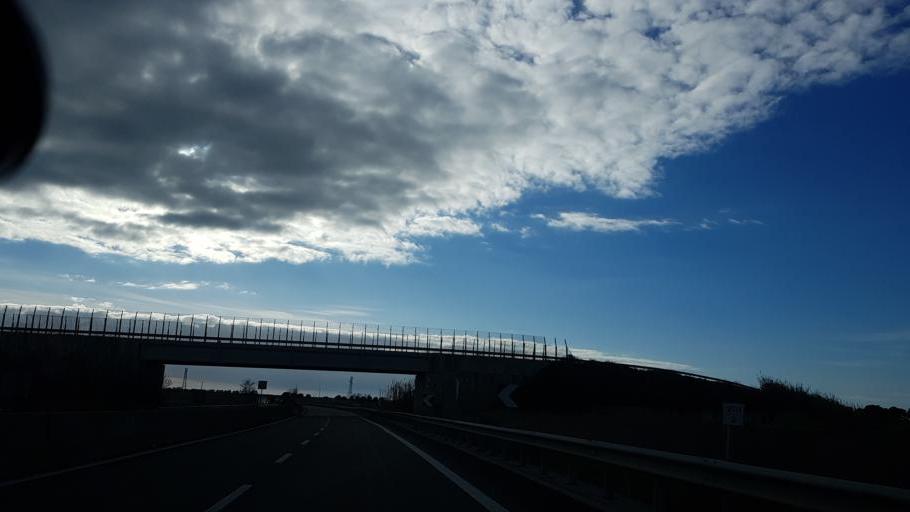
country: IT
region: Apulia
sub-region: Provincia di Brindisi
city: La Rosa
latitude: 40.6003
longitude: 17.9664
